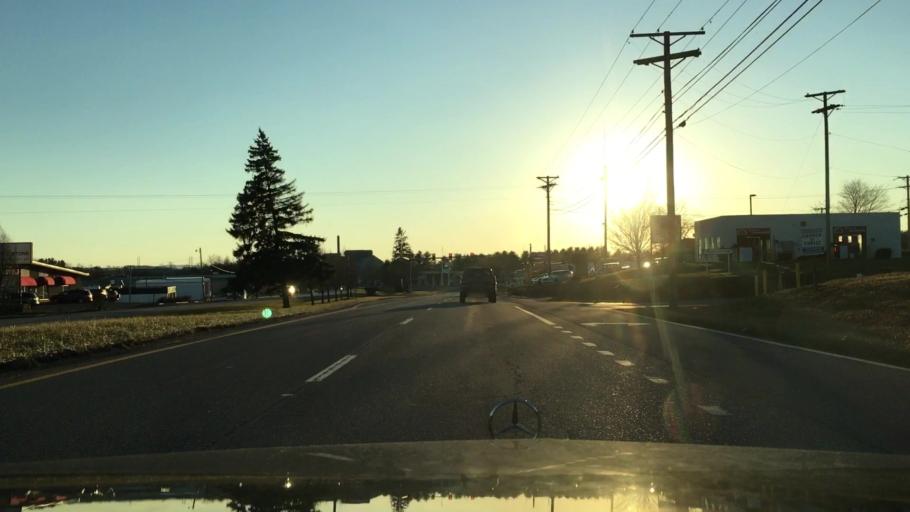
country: US
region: Virginia
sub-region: Montgomery County
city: Merrimac
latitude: 37.1770
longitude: -80.4171
